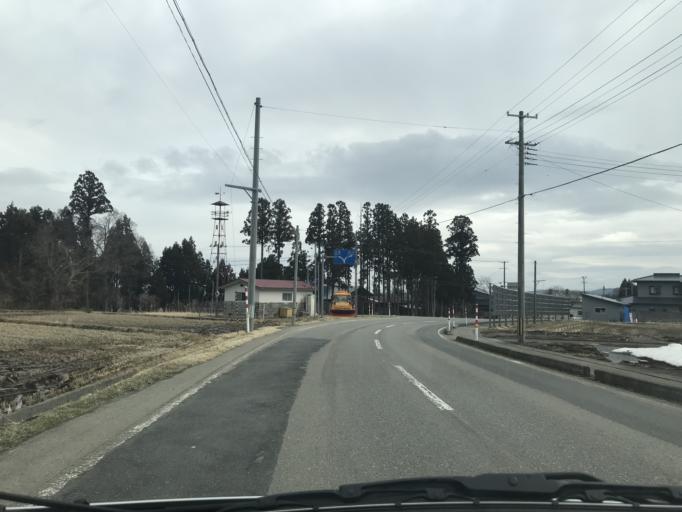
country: JP
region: Iwate
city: Kitakami
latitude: 39.3293
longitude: 140.9767
